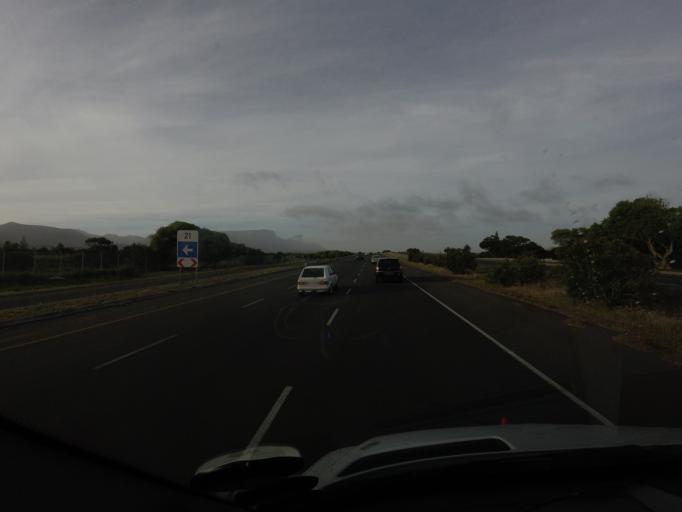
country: ZA
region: Western Cape
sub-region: City of Cape Town
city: Bergvliet
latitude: -34.0677
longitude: 18.4481
